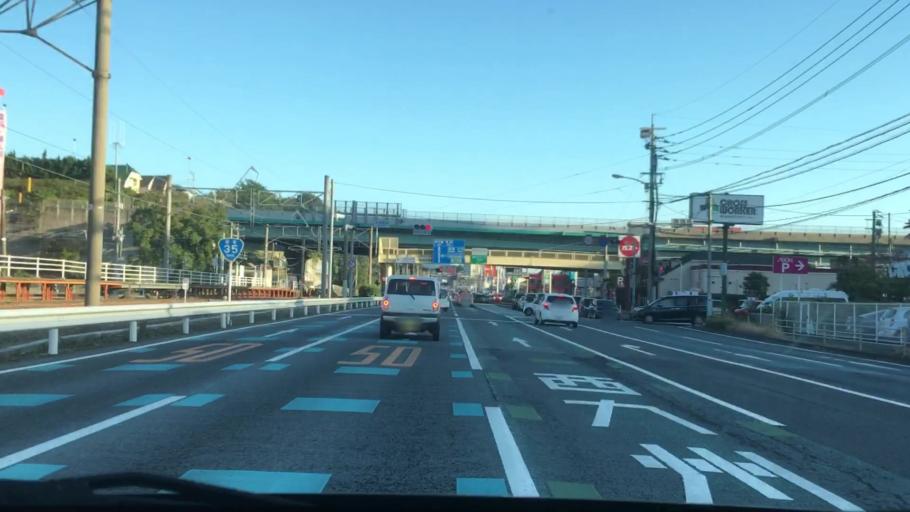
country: JP
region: Nagasaki
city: Sasebo
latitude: 33.1497
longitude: 129.7813
